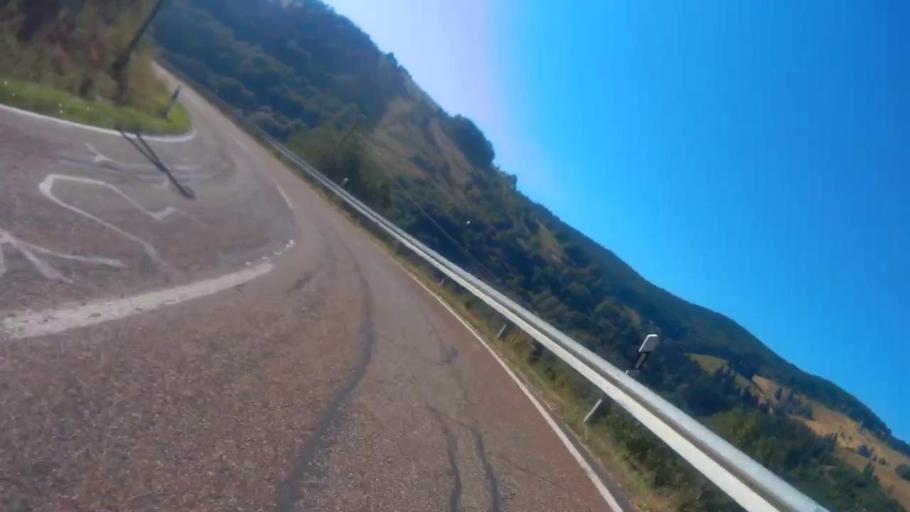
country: DE
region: Baden-Wuerttemberg
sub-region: Freiburg Region
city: Tunau
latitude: 47.7620
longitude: 7.9138
